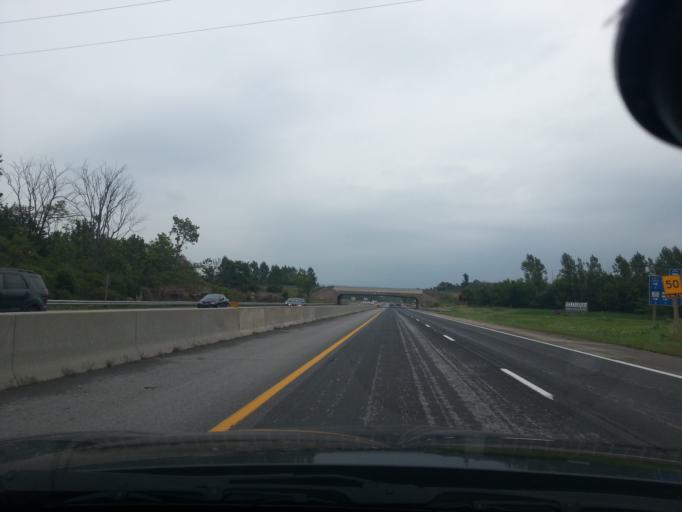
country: CA
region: Ontario
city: Gananoque
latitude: 44.3437
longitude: -76.1739
